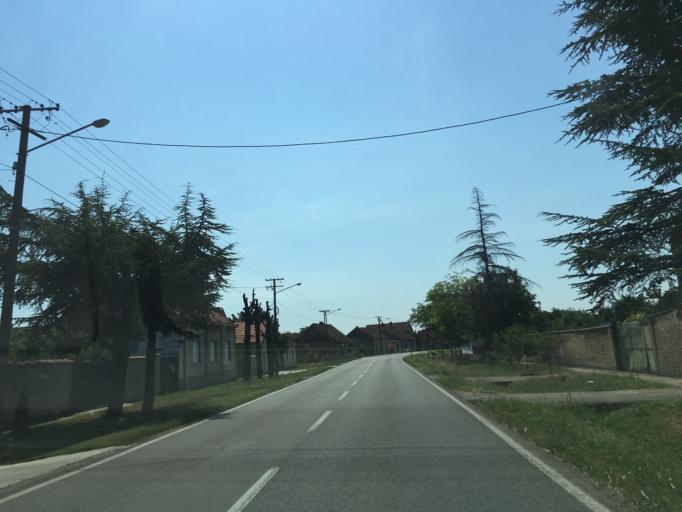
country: RS
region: Autonomna Pokrajina Vojvodina
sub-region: Juznobanatski Okrug
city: Pancevo
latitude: 44.8031
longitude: 20.7137
